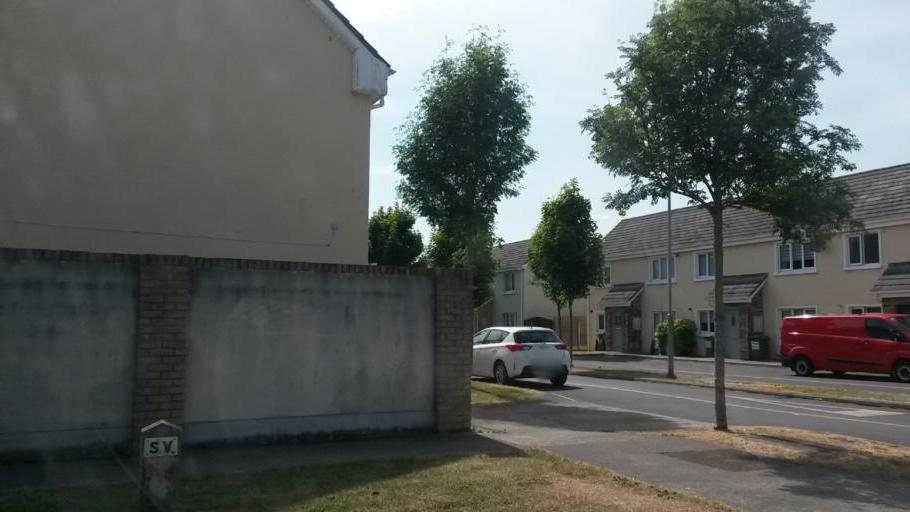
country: IE
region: Leinster
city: Lusk
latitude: 53.5241
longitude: -6.1708
